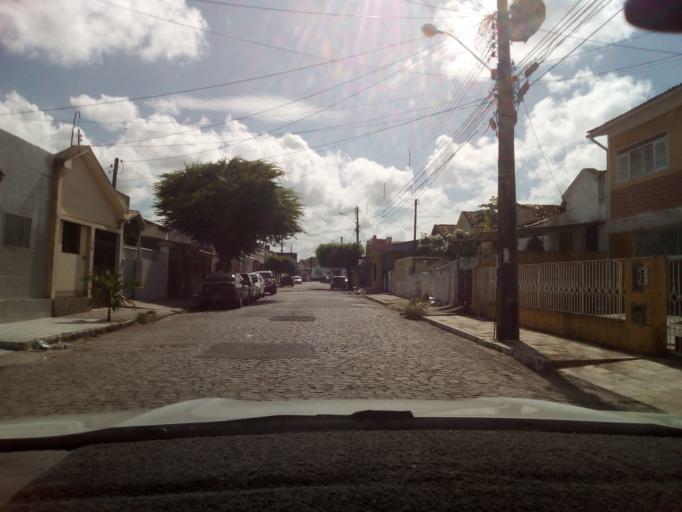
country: BR
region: Paraiba
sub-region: Joao Pessoa
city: Joao Pessoa
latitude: -7.1284
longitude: -34.8810
